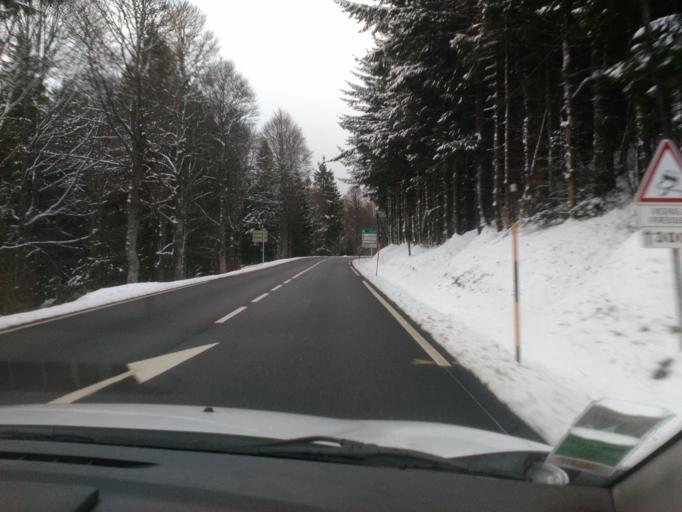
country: FR
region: Alsace
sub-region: Departement du Haut-Rhin
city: Metzeral
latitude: 48.0626
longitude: 7.0166
